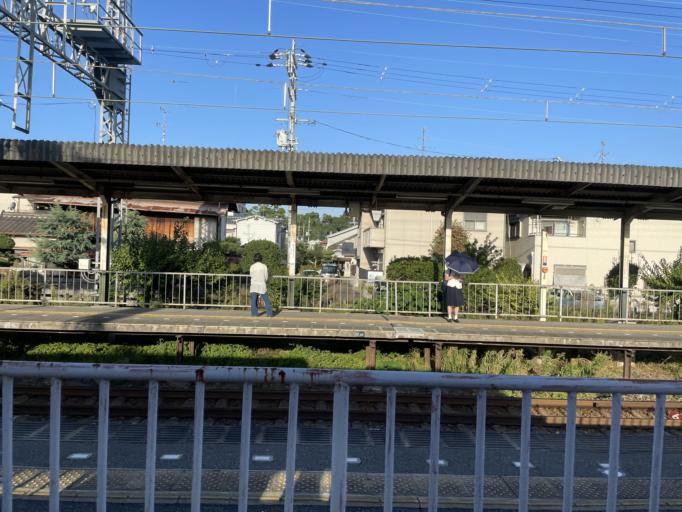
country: JP
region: Osaka
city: Kashihara
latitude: 34.5688
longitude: 135.6204
